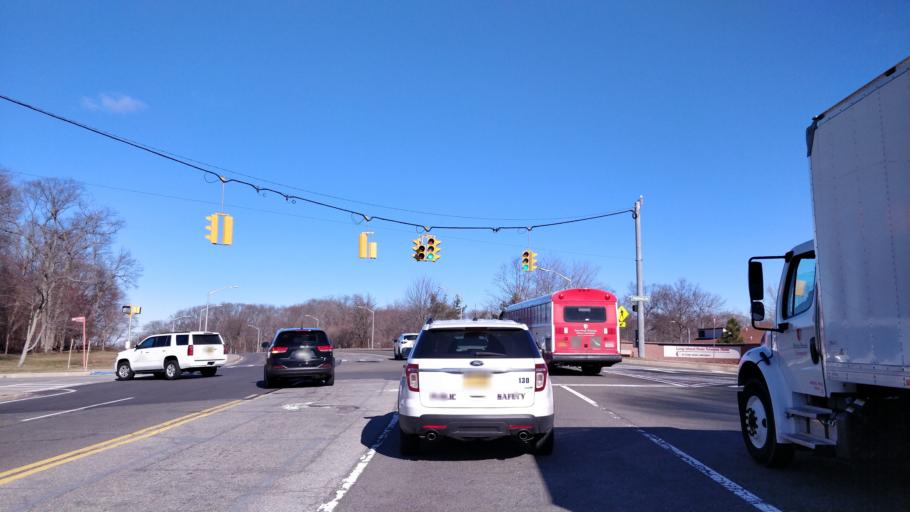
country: US
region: New York
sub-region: Suffolk County
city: Setauket-East Setauket
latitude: 40.9060
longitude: -73.1108
